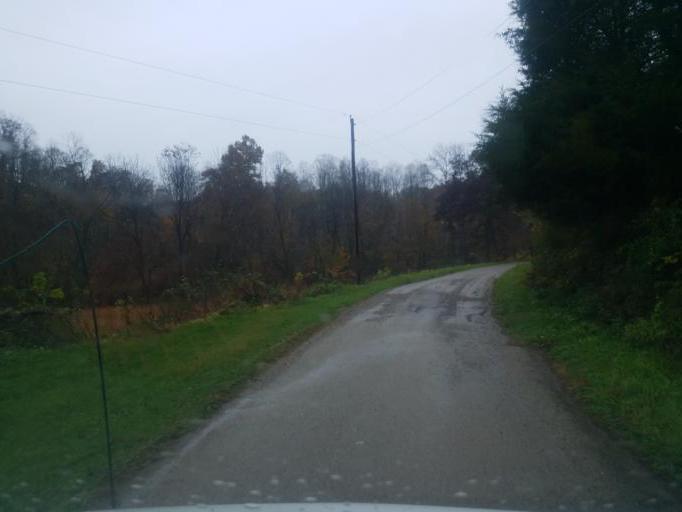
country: US
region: Ohio
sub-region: Washington County
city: Beverly
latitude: 39.4727
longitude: -81.7439
